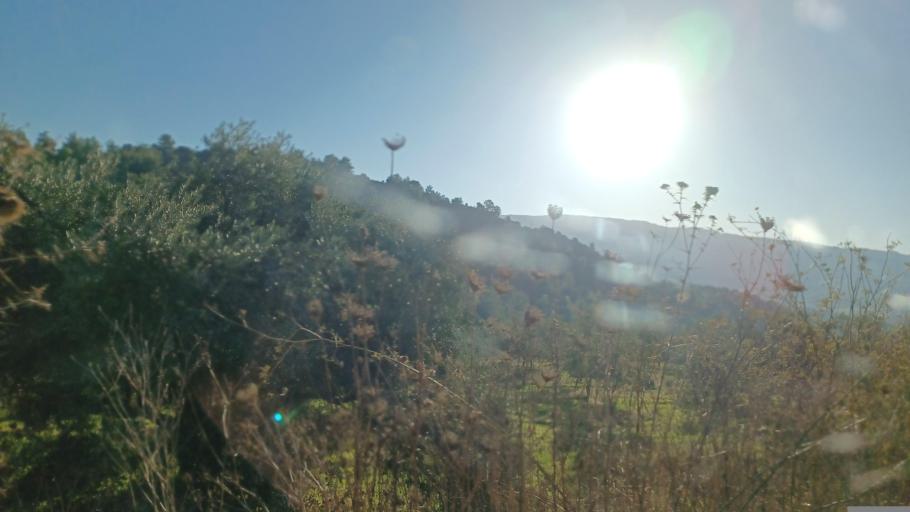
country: CY
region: Pafos
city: Mesogi
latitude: 34.9328
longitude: 32.5678
